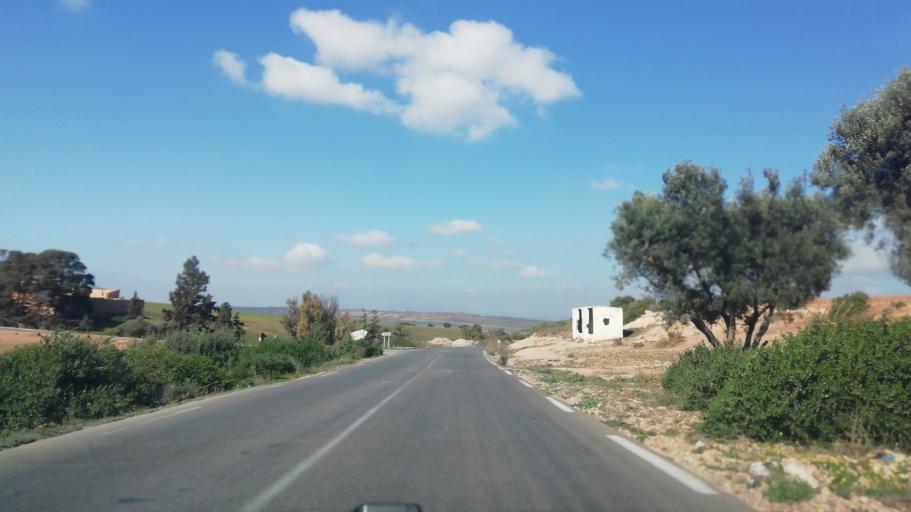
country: DZ
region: Oran
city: Ain el Bya
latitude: 35.7279
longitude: -0.2481
